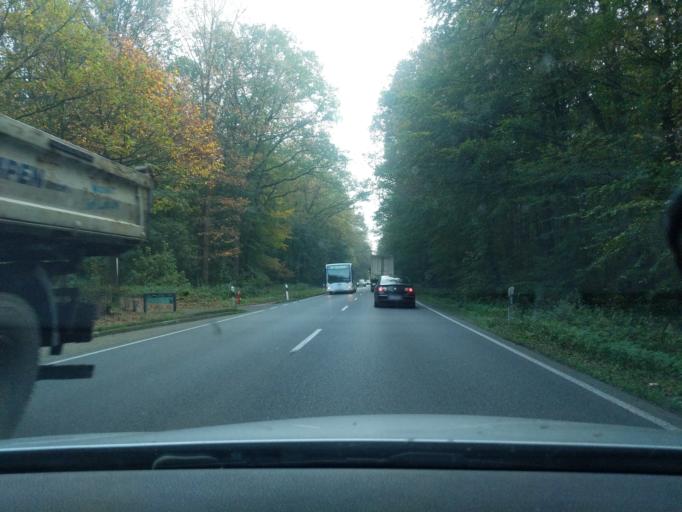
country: DE
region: Lower Saxony
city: Himmelpforten
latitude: 53.6068
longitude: 9.3170
